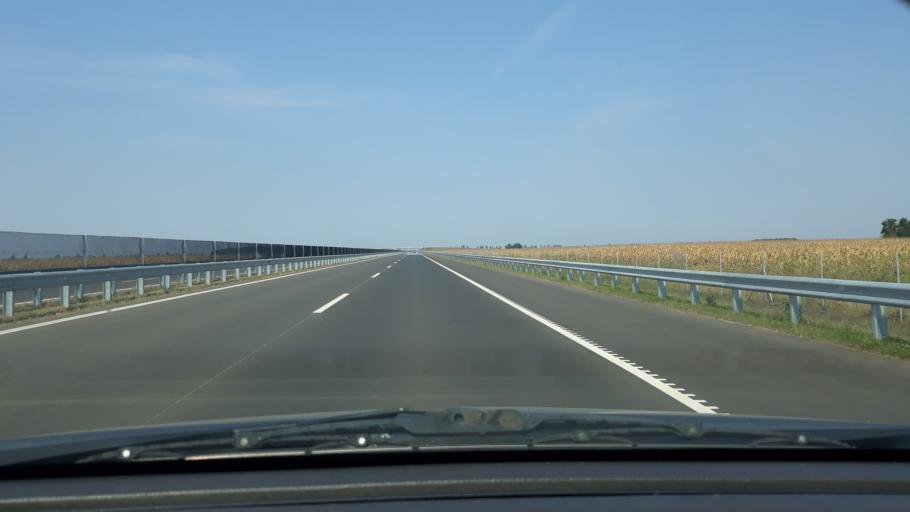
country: HU
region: Hajdu-Bihar
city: Berettyoujfalu
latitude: 47.2539
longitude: 21.5725
